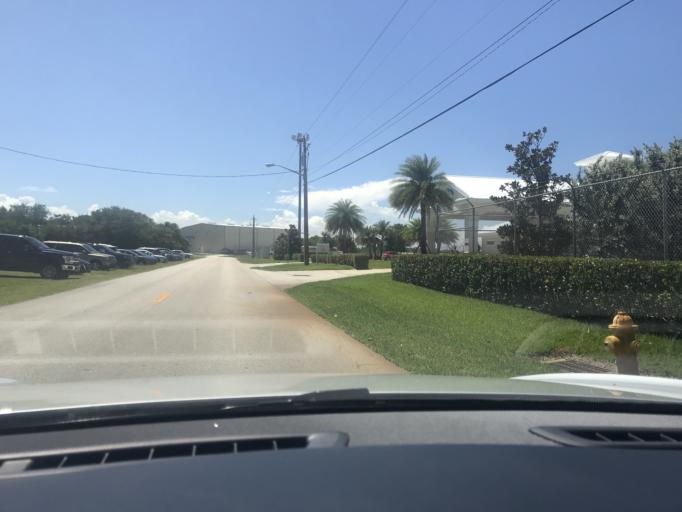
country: US
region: Florida
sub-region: Indian River County
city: Gifford
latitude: 27.6551
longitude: -80.4294
